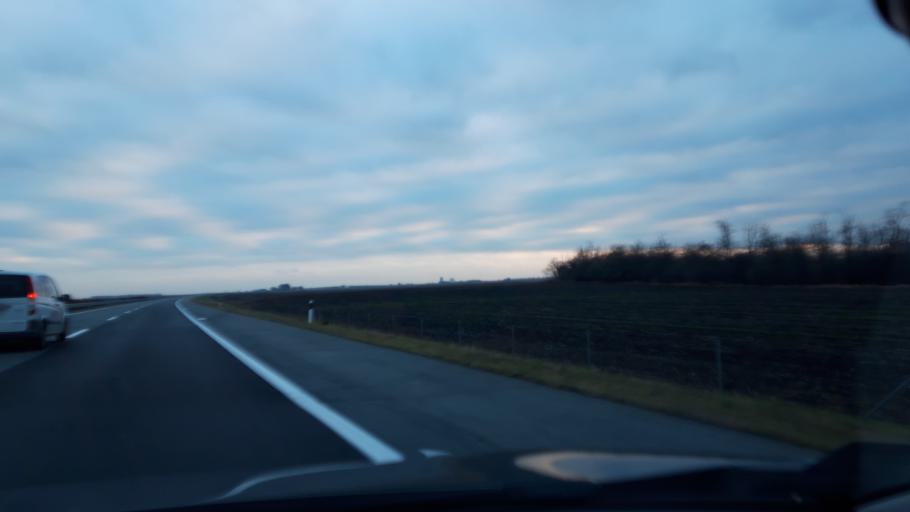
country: RS
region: Autonomna Pokrajina Vojvodina
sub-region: Severnobacki Okrug
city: Mali Igos
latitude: 45.6920
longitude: 19.7248
